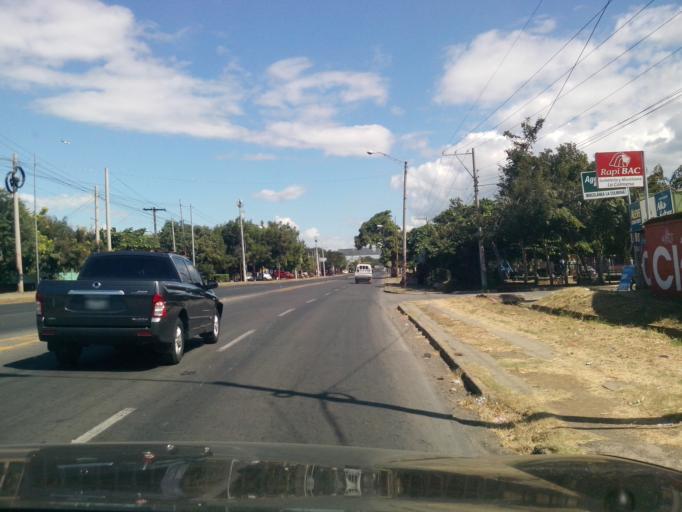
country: NI
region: Managua
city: Ciudad Sandino
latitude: 12.1379
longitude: -86.3065
